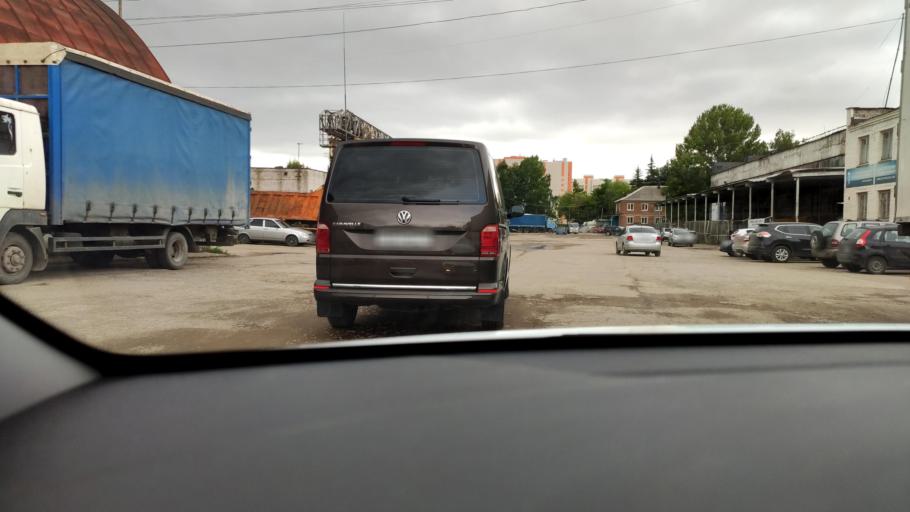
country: RU
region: Tatarstan
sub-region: Gorod Kazan'
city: Kazan
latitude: 55.7689
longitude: 49.1924
